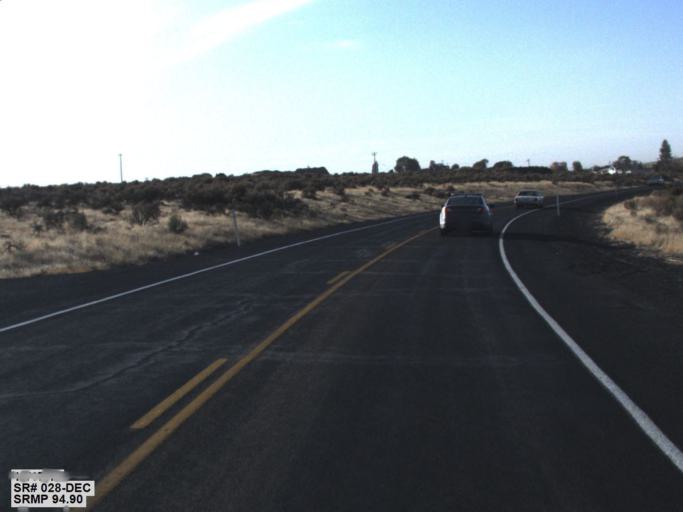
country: US
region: Washington
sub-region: Adams County
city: Ritzville
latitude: 47.3292
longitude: -118.6685
